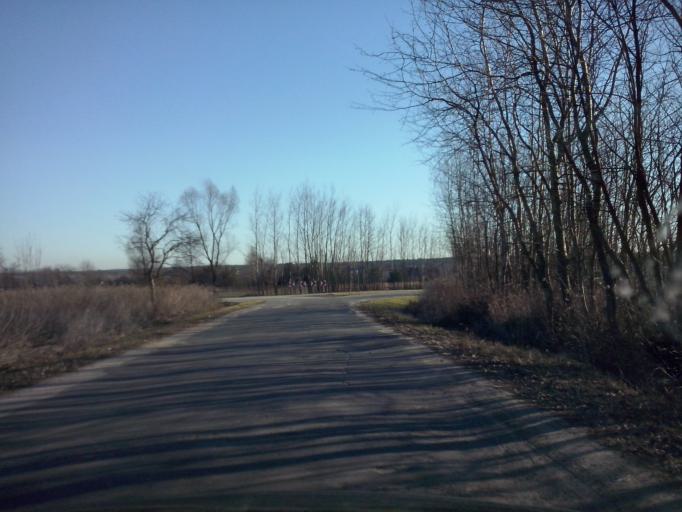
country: PL
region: Subcarpathian Voivodeship
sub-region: Powiat nizanski
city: Harasiuki
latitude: 50.5287
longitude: 22.4469
